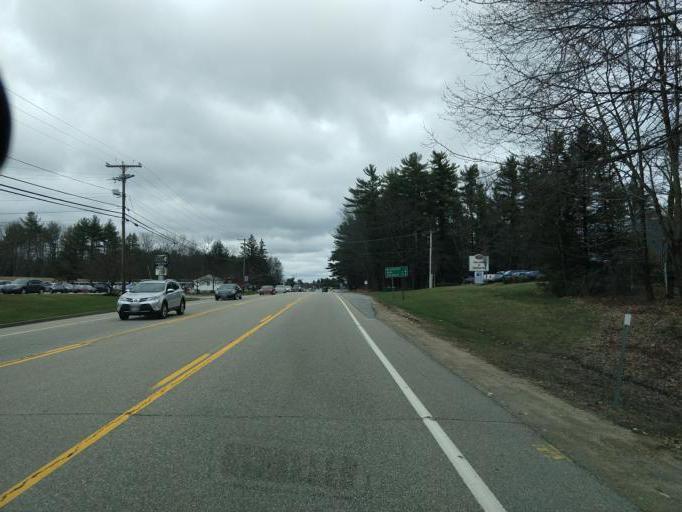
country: US
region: New Hampshire
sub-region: Strafford County
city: Rochester
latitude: 43.3234
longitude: -71.0002
